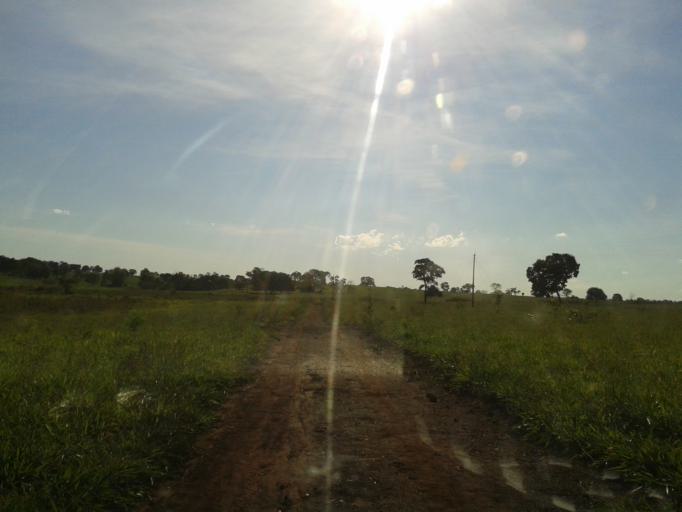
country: BR
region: Minas Gerais
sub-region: Santa Vitoria
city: Santa Vitoria
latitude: -18.9983
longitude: -50.3498
